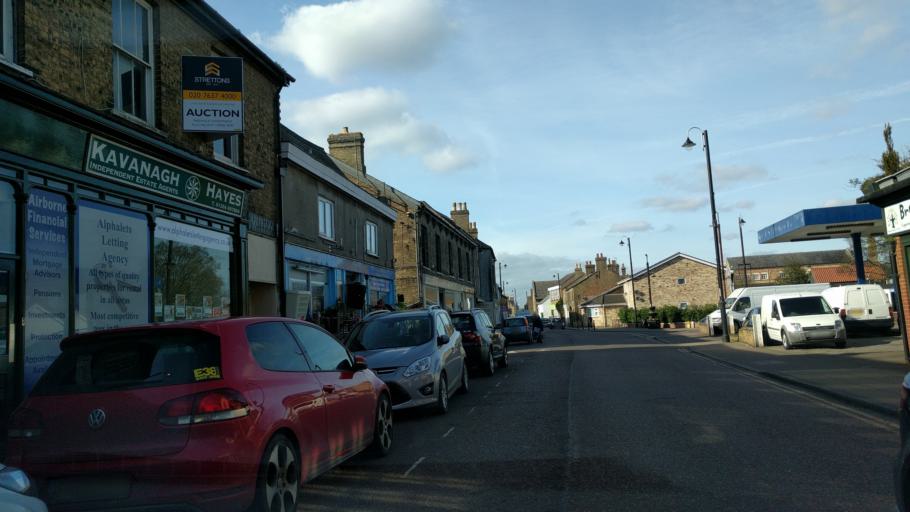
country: GB
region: England
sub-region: Cambridgeshire
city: Chatteris
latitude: 52.4560
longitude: 0.0490
